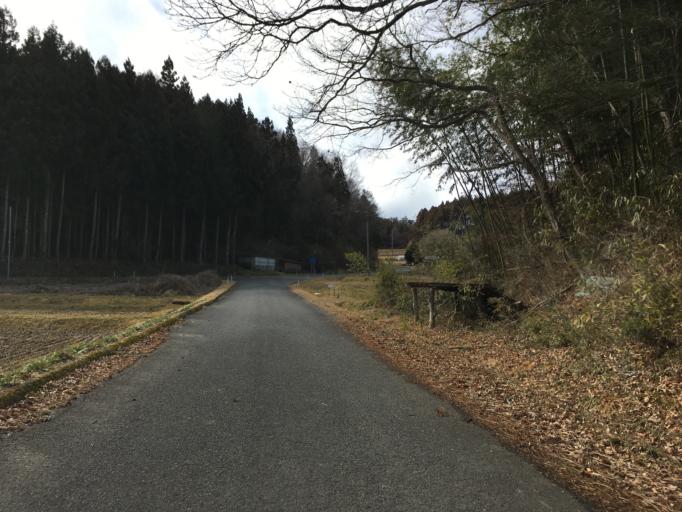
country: JP
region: Fukushima
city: Ishikawa
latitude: 37.2029
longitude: 140.5807
